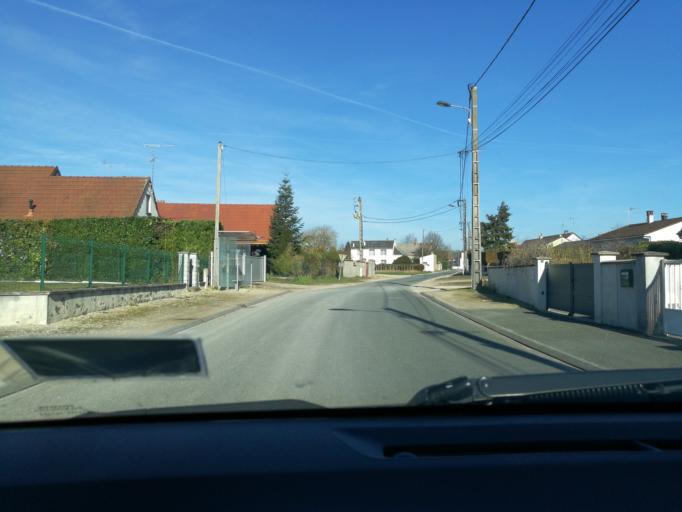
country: FR
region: Centre
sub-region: Departement du Loiret
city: Chaingy
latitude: 47.8870
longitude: 1.7784
